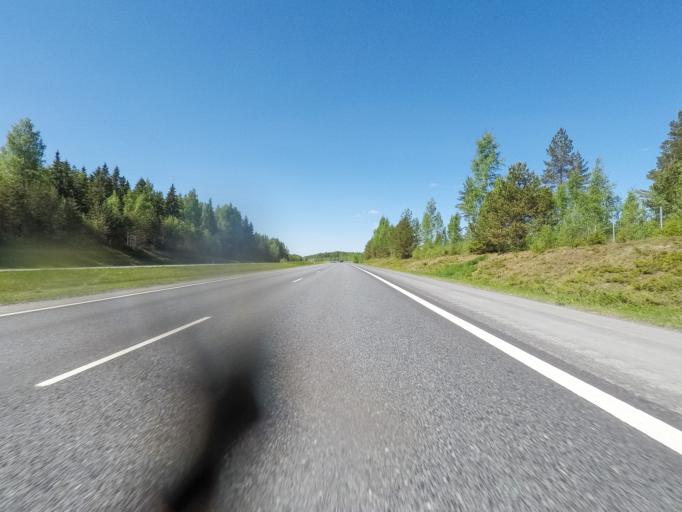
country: FI
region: Haeme
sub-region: Haemeenlinna
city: Kalvola
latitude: 61.1200
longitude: 24.1263
